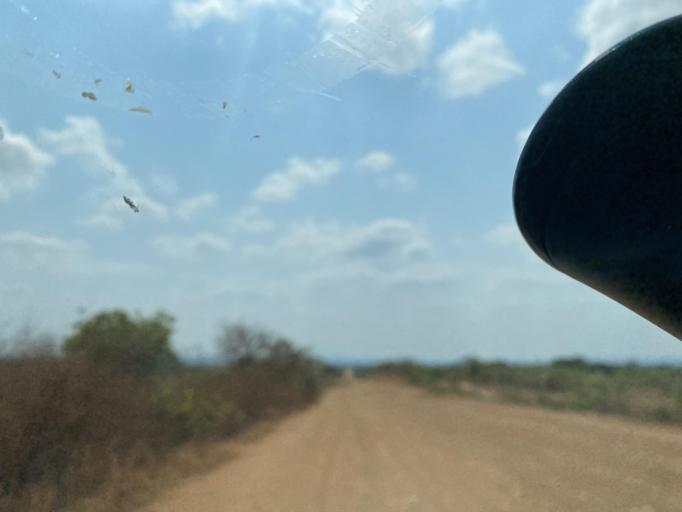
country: ZM
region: Lusaka
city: Chongwe
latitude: -15.5914
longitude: 28.7847
